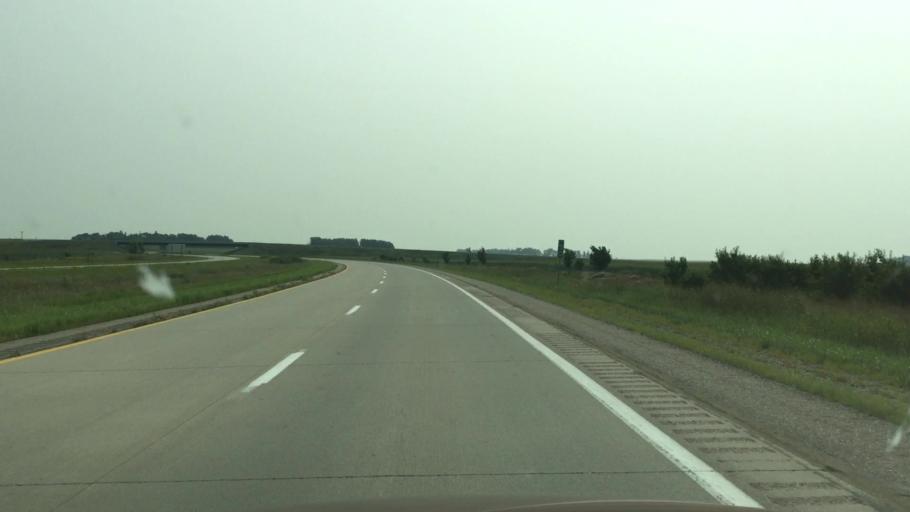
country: US
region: Iowa
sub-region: Osceola County
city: Sibley
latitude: 43.3847
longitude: -95.7291
